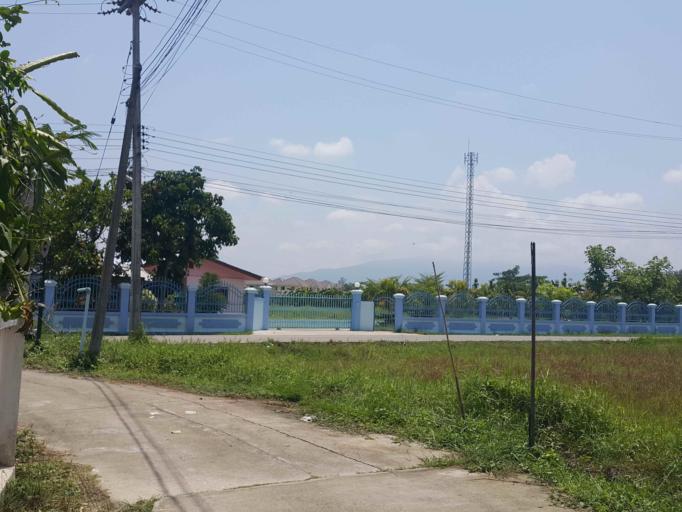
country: TH
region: Chiang Mai
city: San Sai
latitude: 18.8152
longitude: 99.0784
